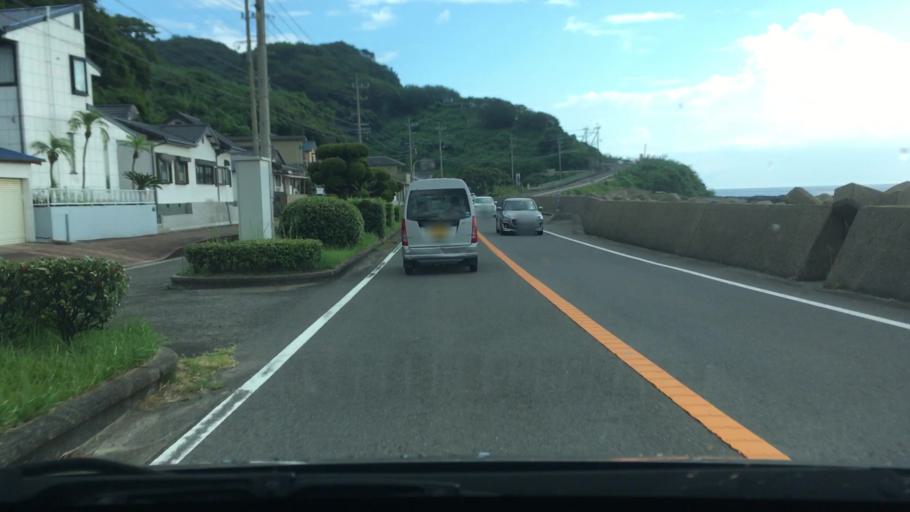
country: JP
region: Nagasaki
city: Togitsu
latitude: 32.8760
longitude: 129.6796
